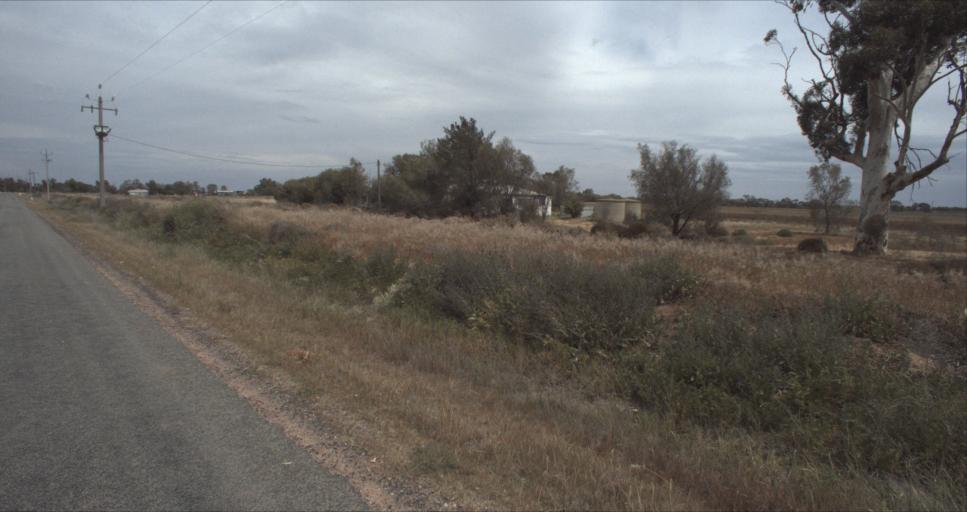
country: AU
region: New South Wales
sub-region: Leeton
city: Leeton
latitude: -34.4375
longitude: 146.3761
